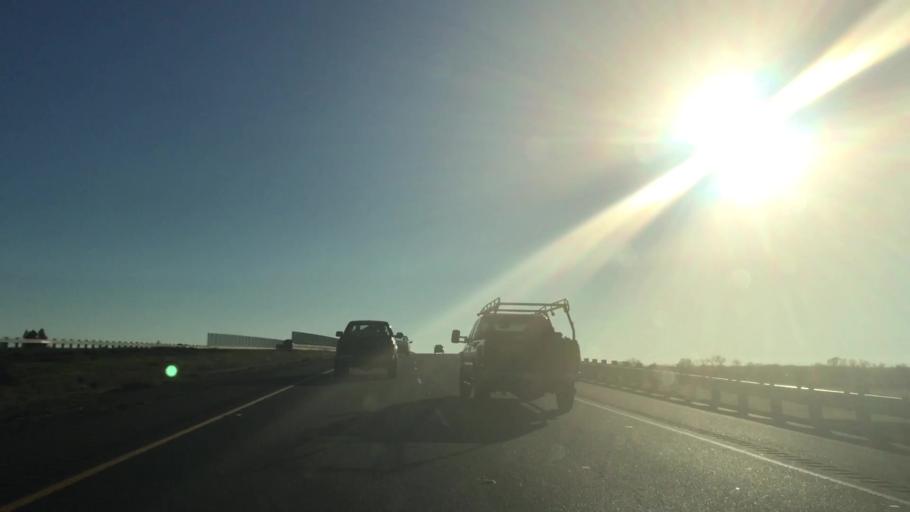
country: US
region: California
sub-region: Yuba County
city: Plumas Lake
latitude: 39.0305
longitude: -121.5449
